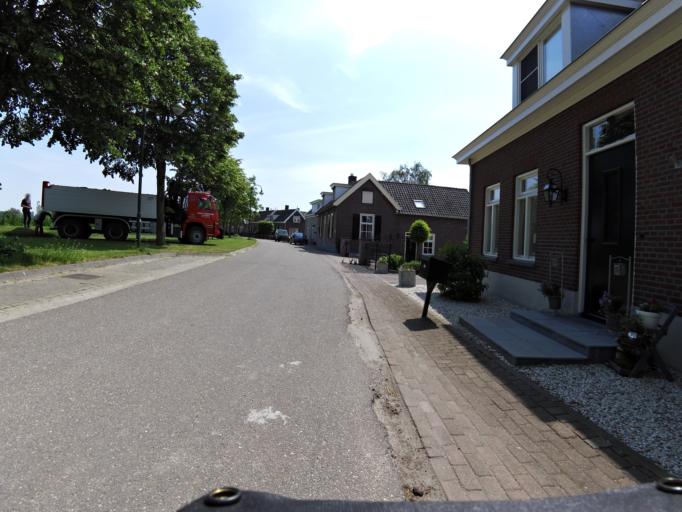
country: NL
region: South Holland
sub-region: Gemeente Leerdam
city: Leerdam
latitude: 51.8218
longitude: 5.0887
